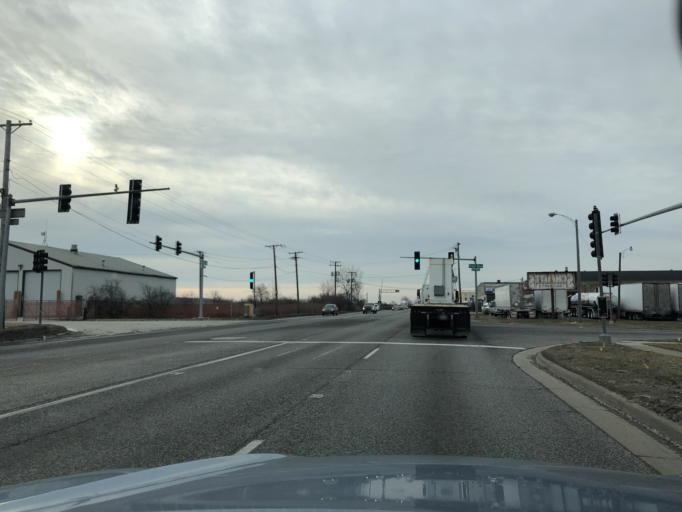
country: US
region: Illinois
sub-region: Cook County
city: Elk Grove Village
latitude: 41.9991
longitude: -87.9401
